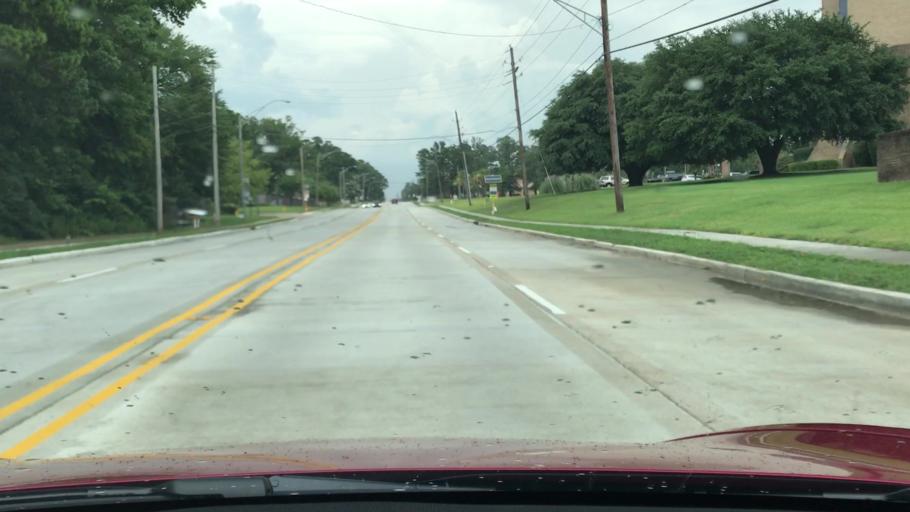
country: US
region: Louisiana
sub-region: Bossier Parish
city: Bossier City
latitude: 32.4033
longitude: -93.7633
